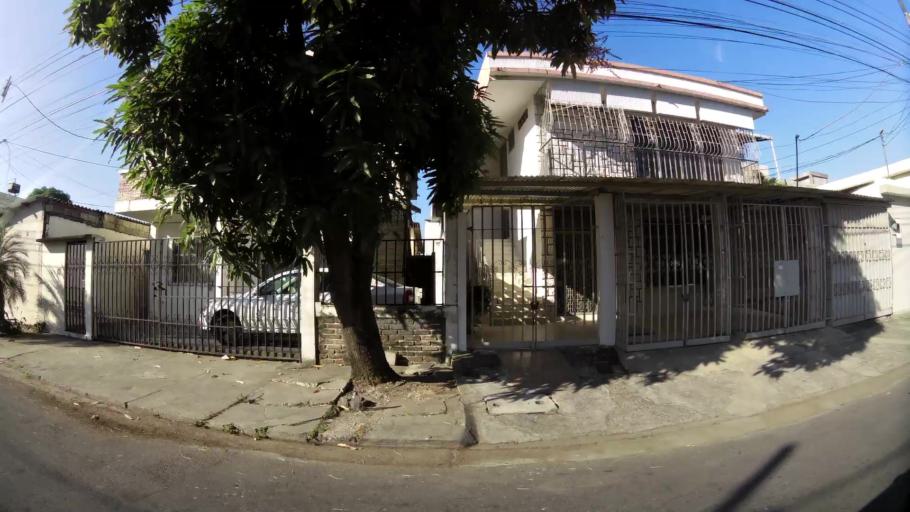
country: EC
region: Guayas
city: Eloy Alfaro
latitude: -2.1671
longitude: -79.8846
